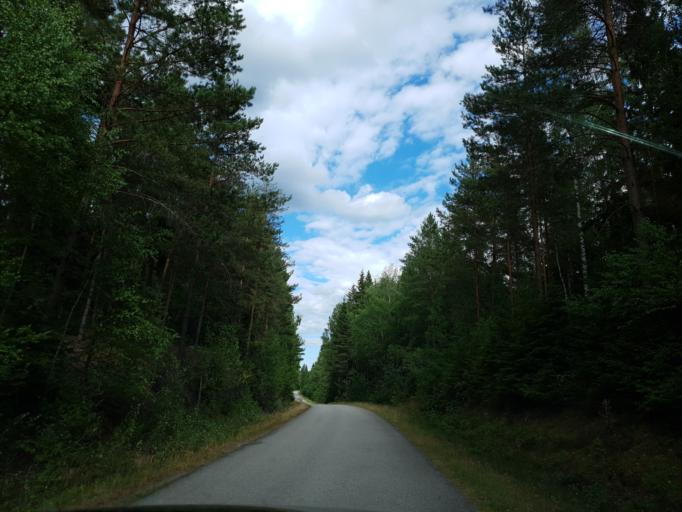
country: SE
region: Kalmar
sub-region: Emmaboda Kommun
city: Emmaboda
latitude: 56.6226
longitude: 15.6506
